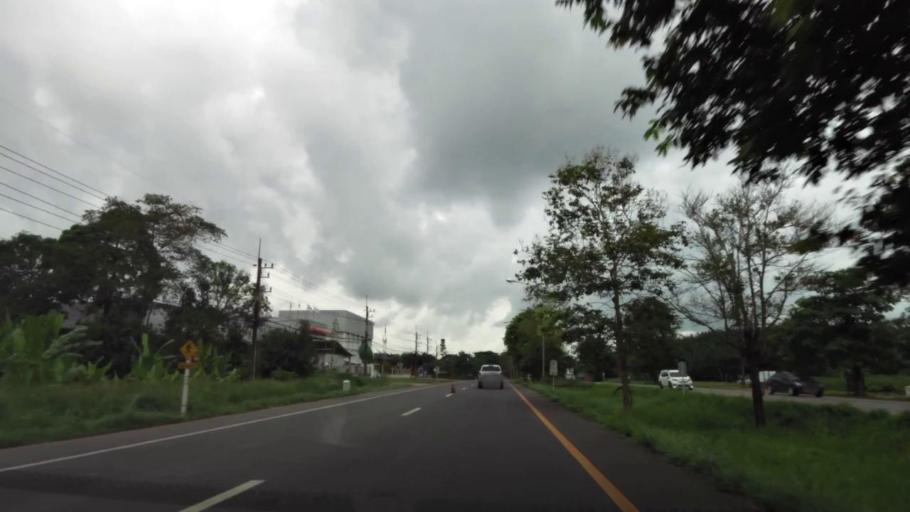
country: TH
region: Chanthaburi
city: Tha Mai
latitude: 12.6711
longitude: 102.0062
